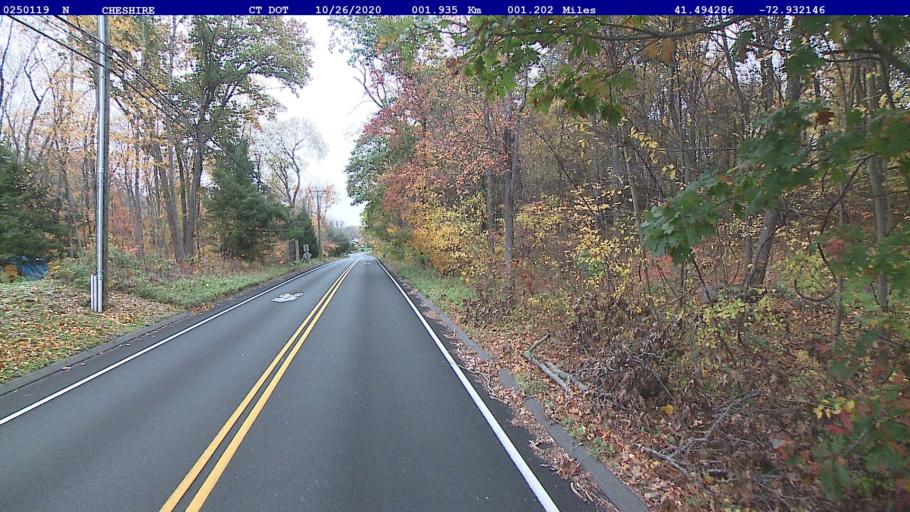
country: US
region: Connecticut
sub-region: New Haven County
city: Cheshire
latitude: 41.4943
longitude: -72.9321
